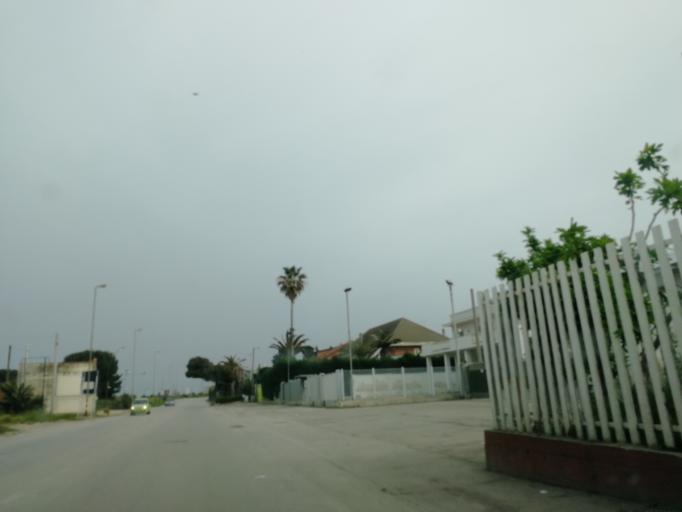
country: IT
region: Apulia
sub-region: Provincia di Barletta - Andria - Trani
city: Barletta
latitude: 41.3161
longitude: 16.2983
